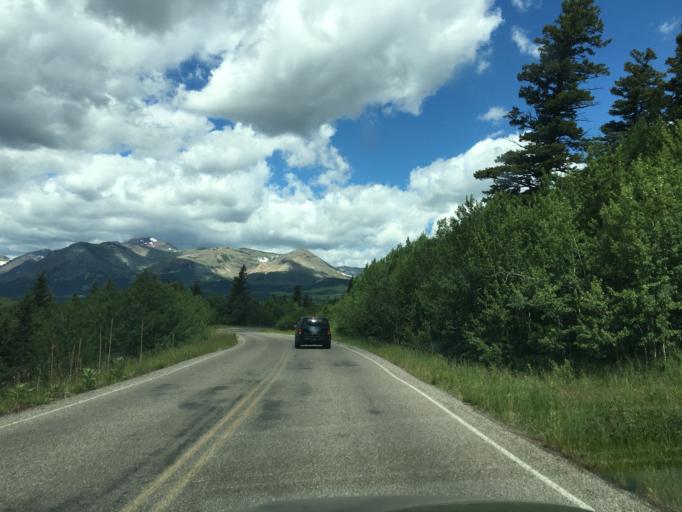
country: US
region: Montana
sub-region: Glacier County
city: South Browning
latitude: 48.4959
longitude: -113.2656
